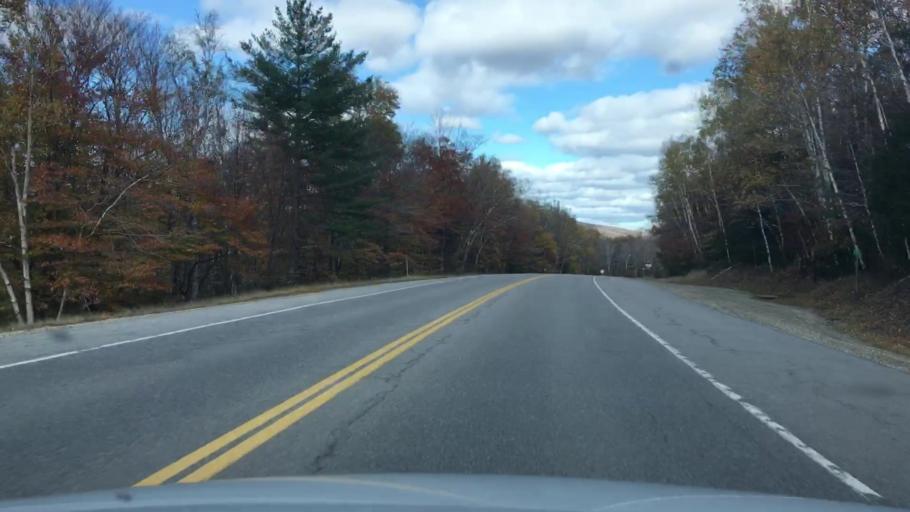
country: US
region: New Hampshire
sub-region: Coos County
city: Gorham
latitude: 44.3230
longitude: -71.2173
